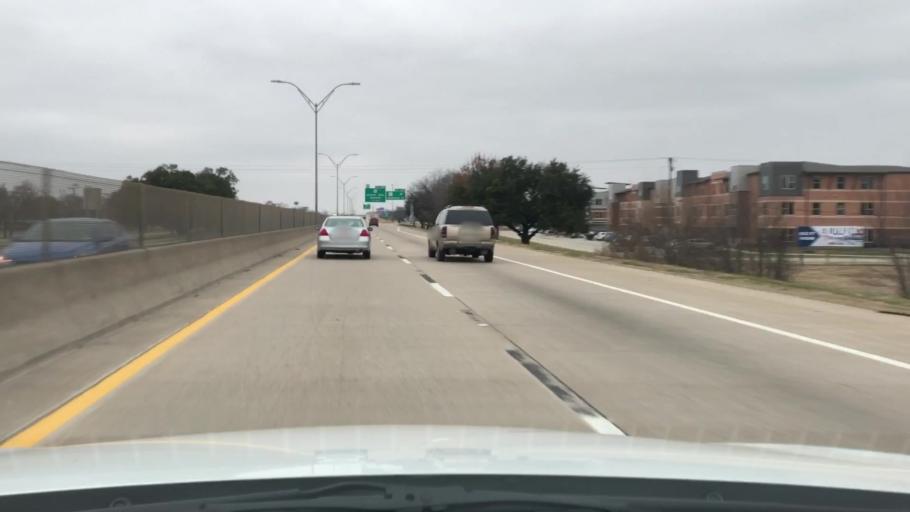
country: US
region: Texas
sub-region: Cooke County
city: Gainesville
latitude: 33.6194
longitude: -97.1502
